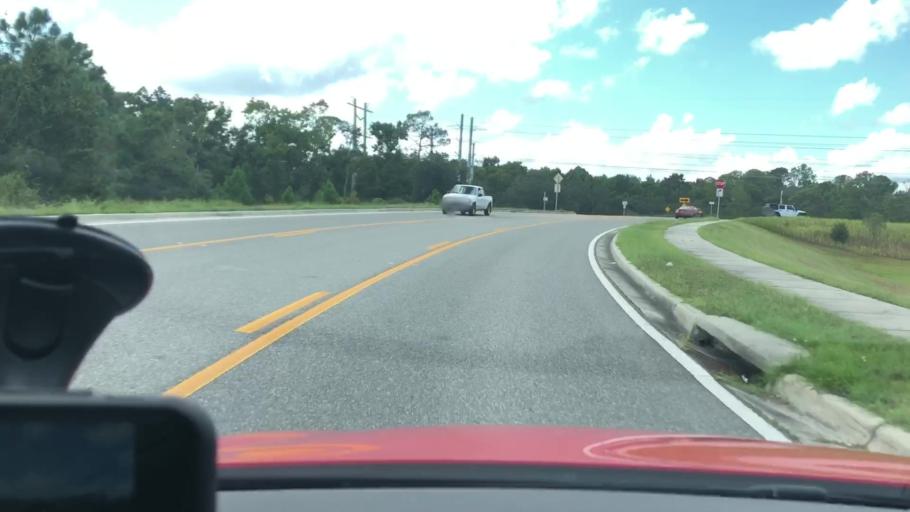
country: US
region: Florida
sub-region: Volusia County
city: Daytona Beach
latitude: 29.1959
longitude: -81.0962
